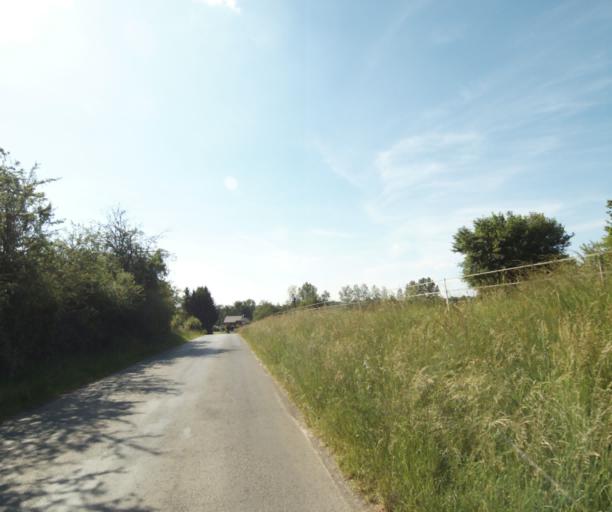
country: FR
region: Champagne-Ardenne
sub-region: Departement des Ardennes
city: Warcq
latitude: 49.7924
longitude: 4.6852
